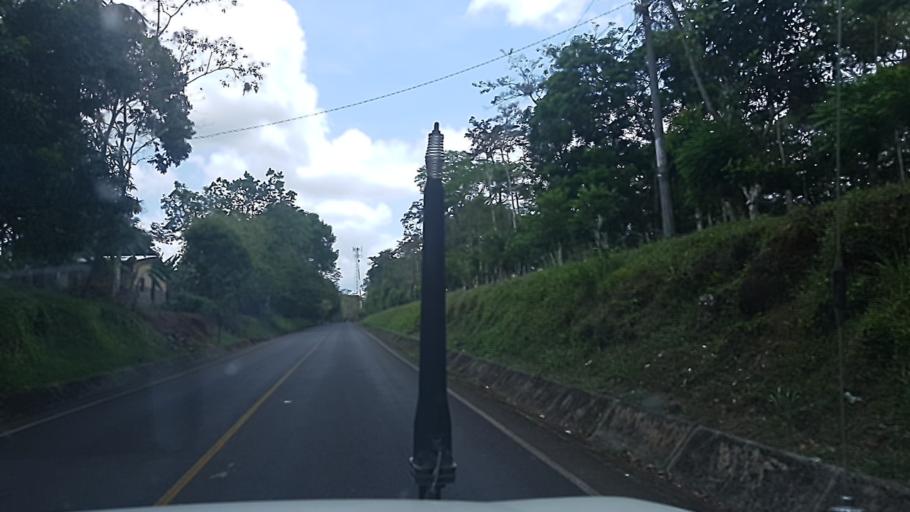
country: NI
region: Atlantico Sur
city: Muelle de los Bueyes
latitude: 11.8880
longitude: -84.6444
